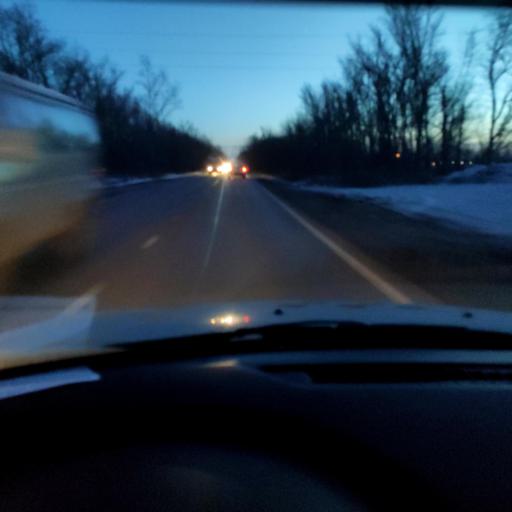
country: RU
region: Samara
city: Tol'yatti
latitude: 53.5506
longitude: 49.3937
